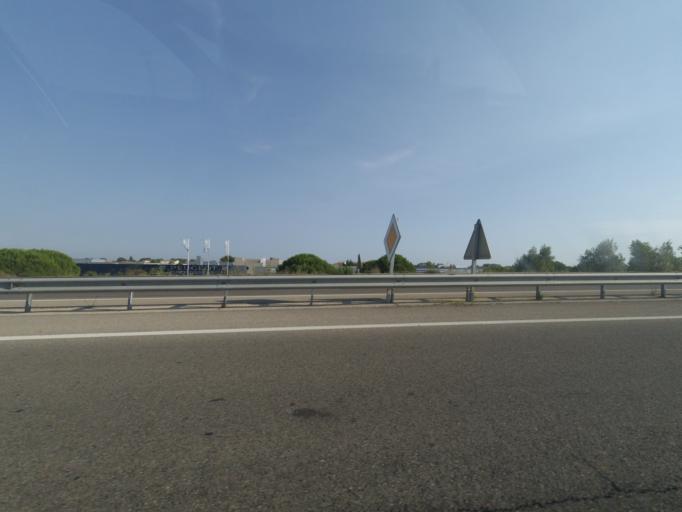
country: FR
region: Languedoc-Roussillon
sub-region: Departement du Gard
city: Aigues-Mortes
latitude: 43.5778
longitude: 4.1842
